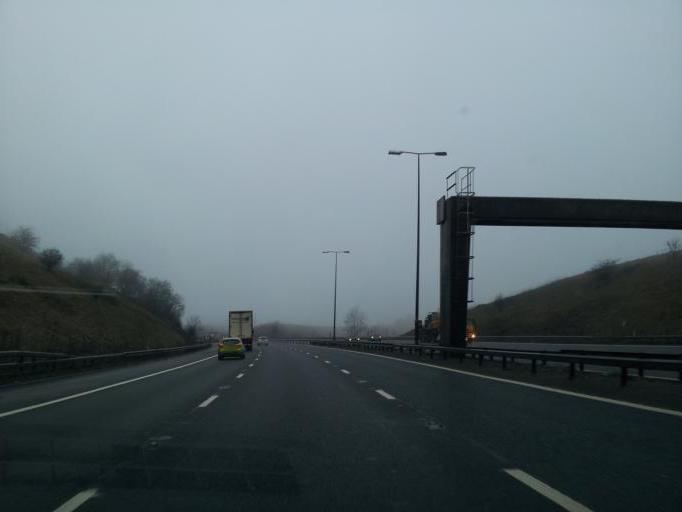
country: GB
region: England
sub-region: Borough of Rochdale
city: Littleborough
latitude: 53.6193
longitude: -2.0850
